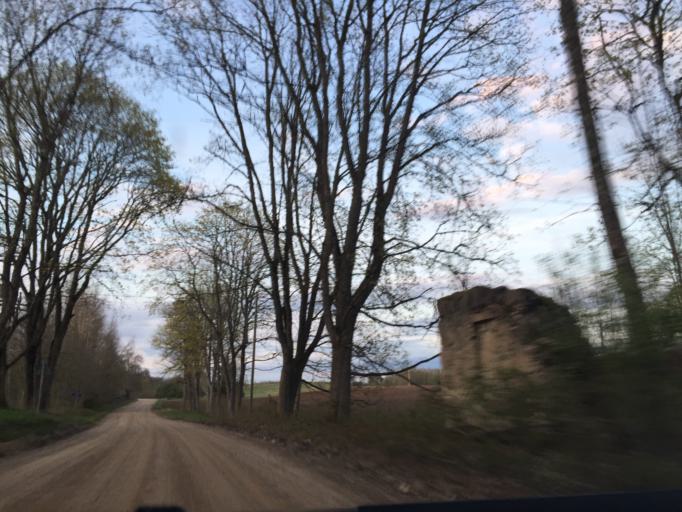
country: LV
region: Aluksnes Rajons
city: Aluksne
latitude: 57.3184
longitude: 26.9293
